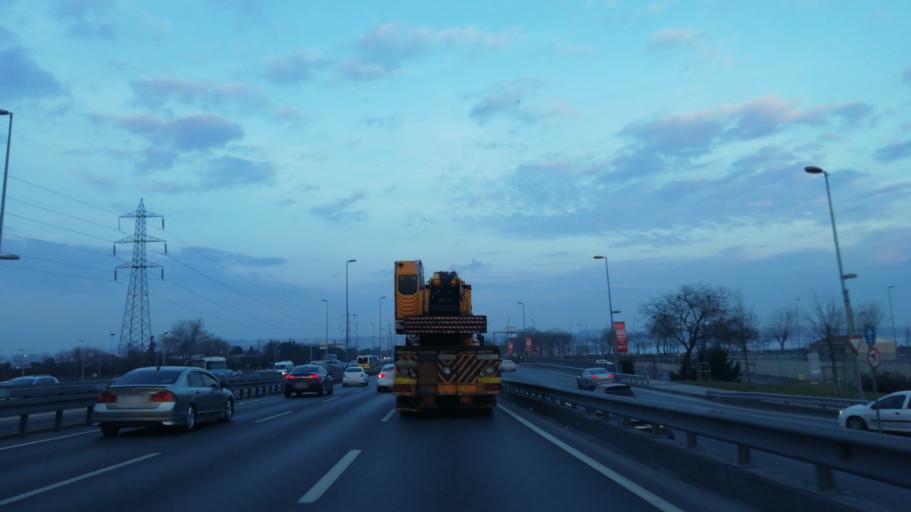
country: TR
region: Istanbul
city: Yakuplu
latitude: 40.9789
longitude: 28.7482
